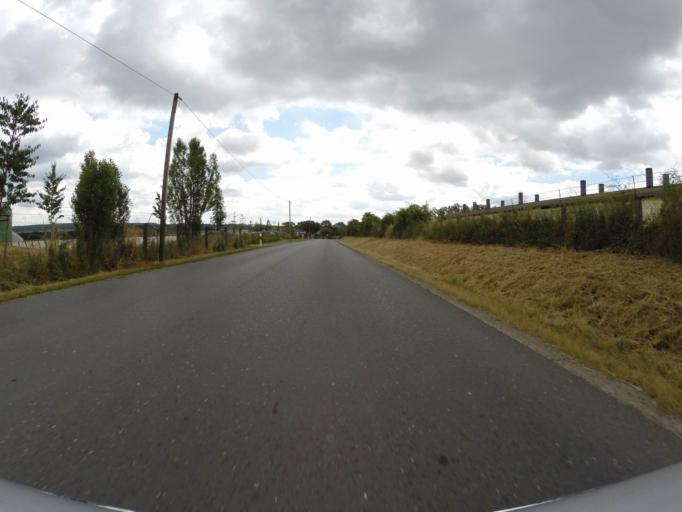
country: DE
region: Thuringia
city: Schongleina
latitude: 50.9223
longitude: 11.7303
